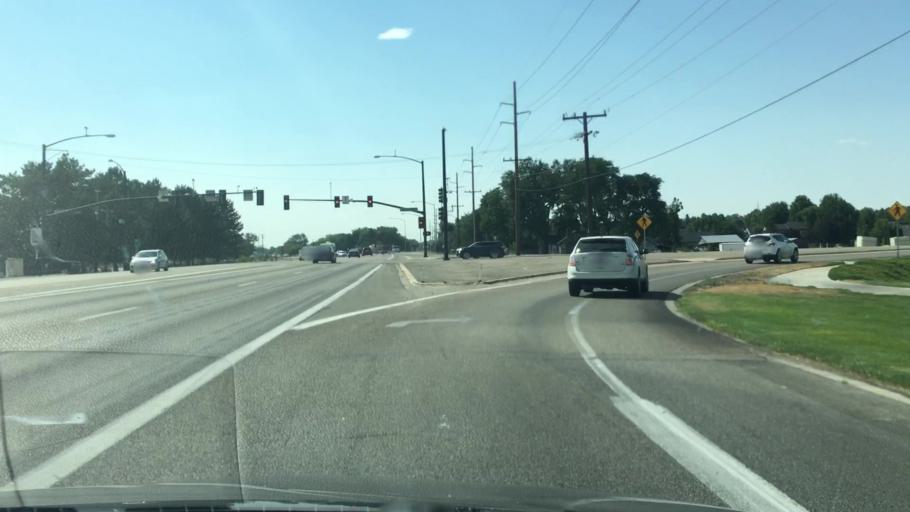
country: US
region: Idaho
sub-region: Ada County
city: Eagle
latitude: 43.6844
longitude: -116.3191
